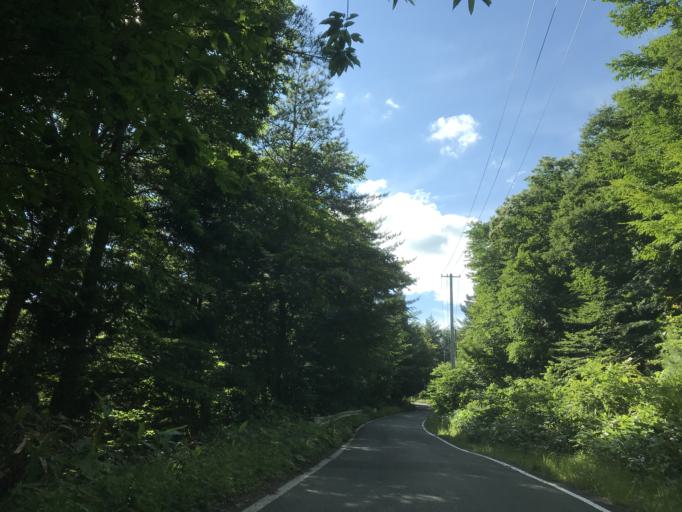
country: JP
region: Iwate
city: Ichinoseki
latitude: 38.8967
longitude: 140.8878
